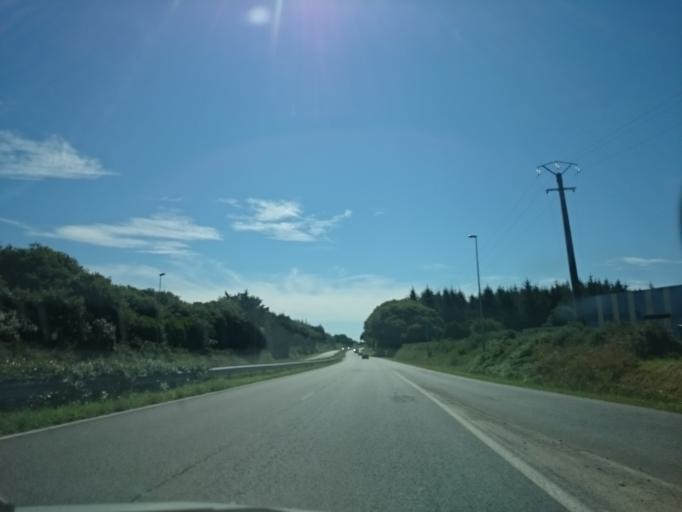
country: FR
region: Brittany
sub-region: Departement du Finistere
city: Guilers
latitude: 48.4246
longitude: -4.5703
